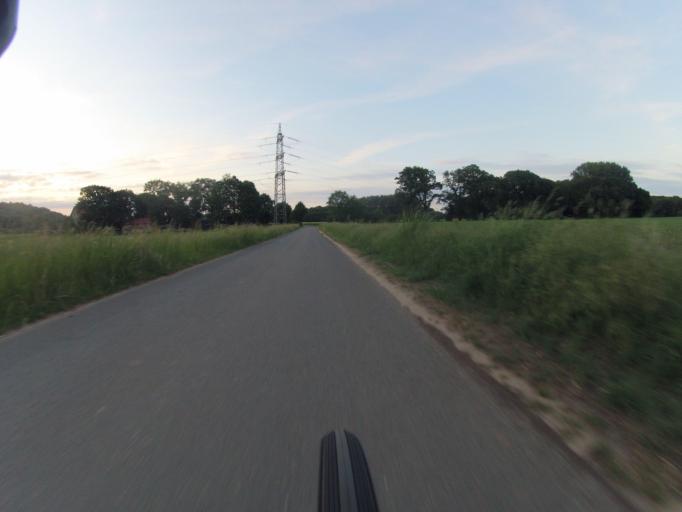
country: DE
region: North Rhine-Westphalia
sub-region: Regierungsbezirk Munster
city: Tecklenburg
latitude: 52.2499
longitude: 7.8128
